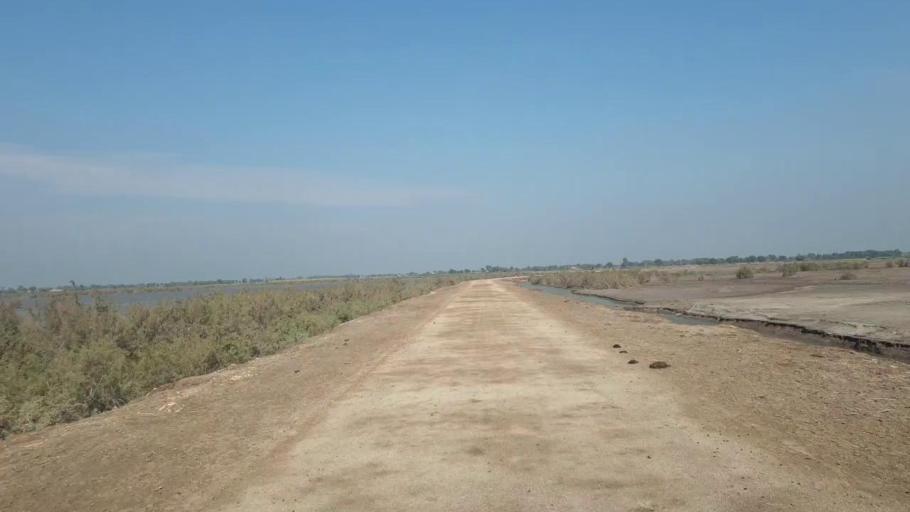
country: PK
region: Sindh
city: Shahdadpur
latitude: 25.9785
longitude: 68.5106
